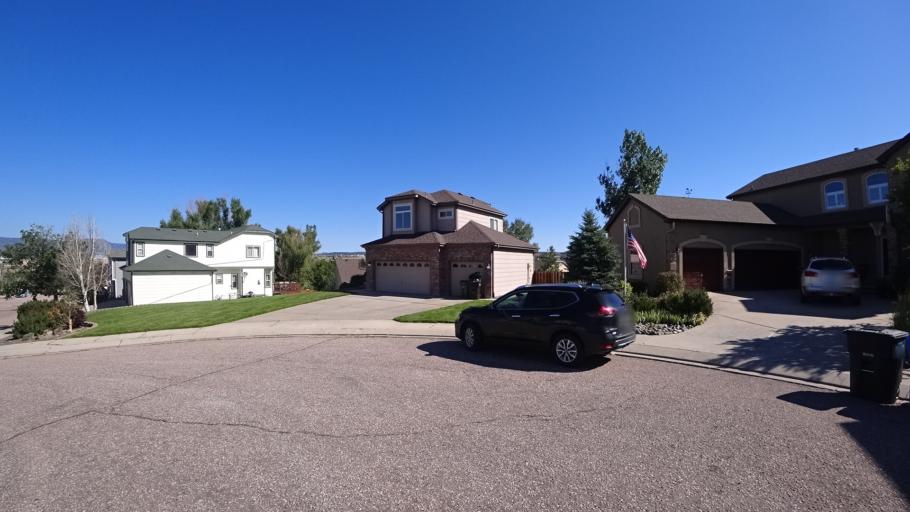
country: US
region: Colorado
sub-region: El Paso County
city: Gleneagle
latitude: 38.9801
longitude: -104.7780
